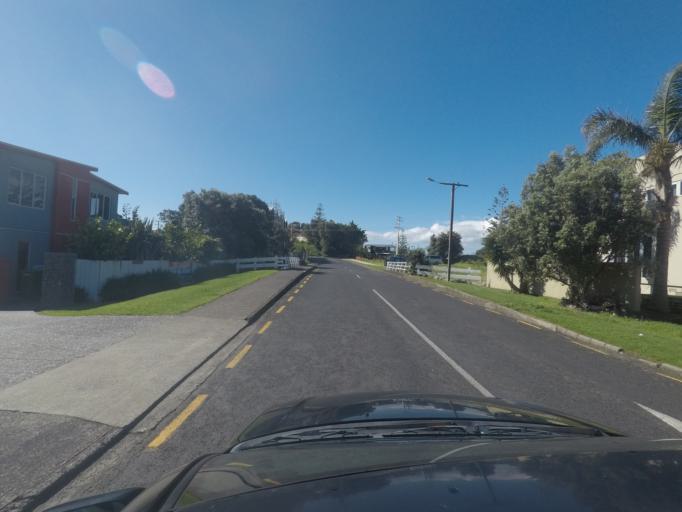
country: NZ
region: Bay of Plenty
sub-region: Western Bay of Plenty District
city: Waihi Beach
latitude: -37.4120
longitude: 175.9447
